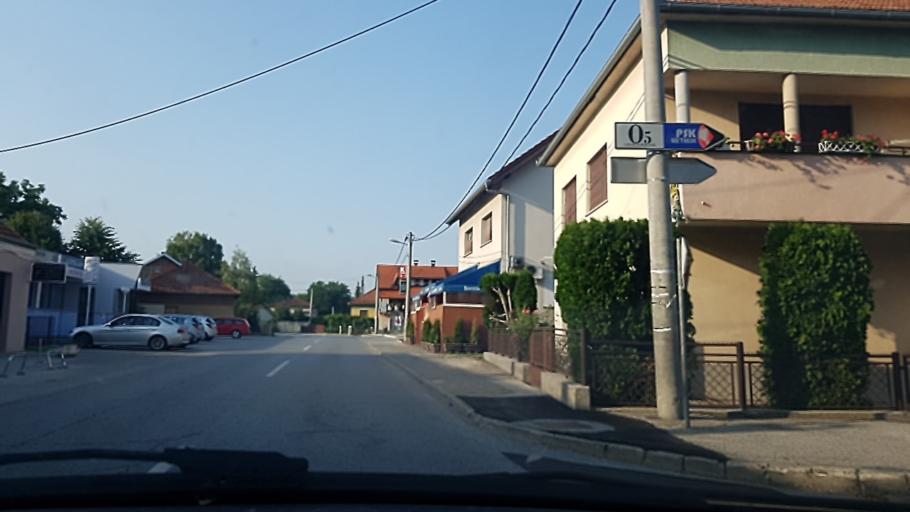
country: HR
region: Zagrebacka
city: Jakovlje
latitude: 45.9950
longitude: 15.8456
